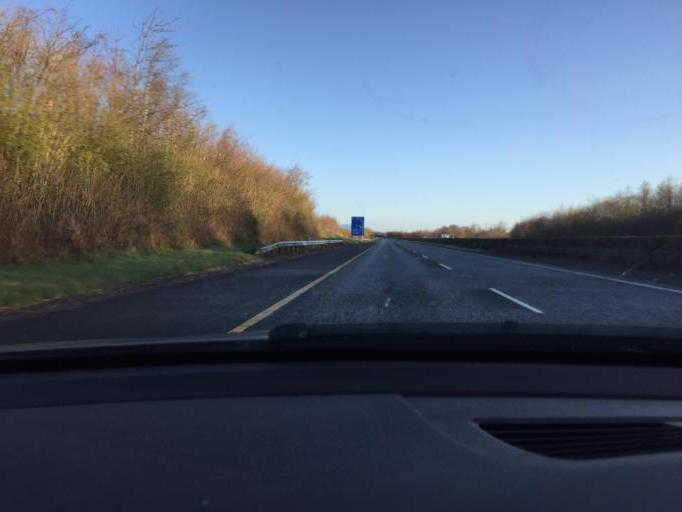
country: IE
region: Leinster
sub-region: Lu
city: Dromiskin
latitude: 53.9527
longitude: -6.4194
